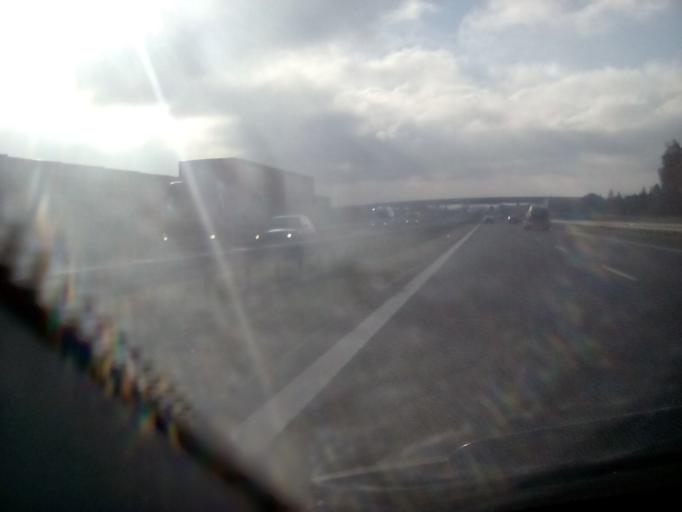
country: PL
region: Masovian Voivodeship
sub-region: Powiat bialobrzeski
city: Promna
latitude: 51.7121
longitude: 20.9247
